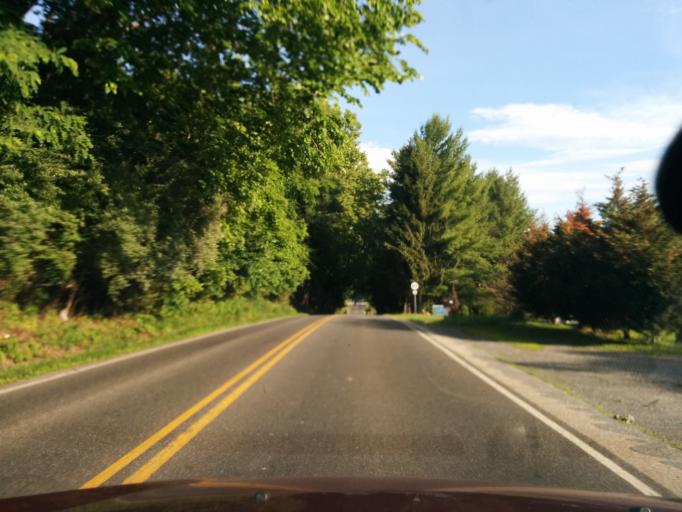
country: US
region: Virginia
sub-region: City of Lexington
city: Lexington
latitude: 37.8064
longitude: -79.4708
